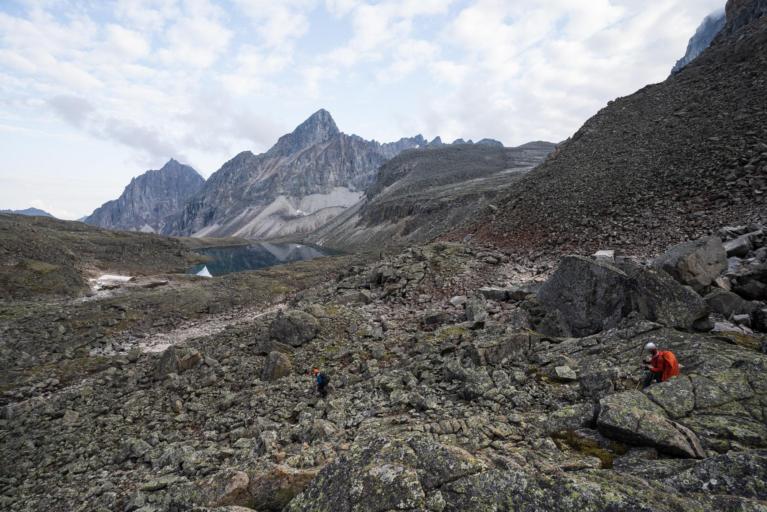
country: RU
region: Transbaikal Territory
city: Chara
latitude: 56.8767
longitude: 117.5943
